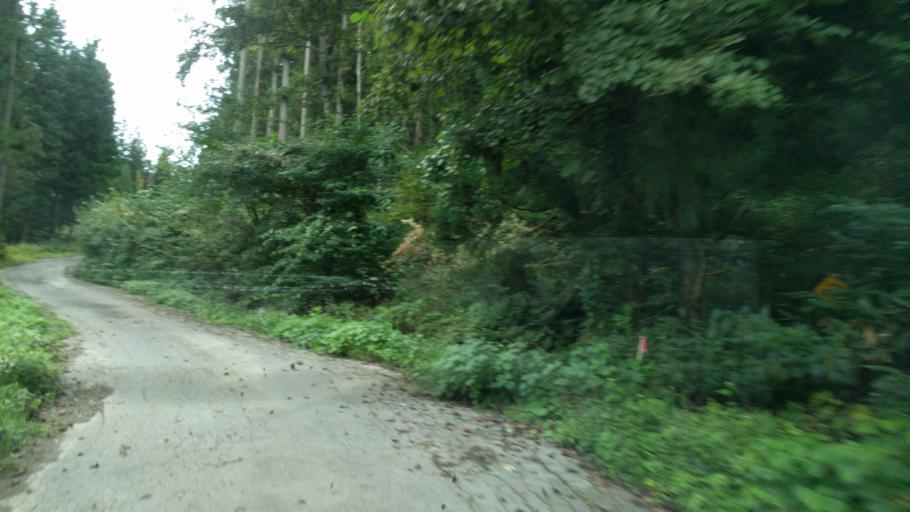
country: JP
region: Fukushima
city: Kitakata
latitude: 37.5217
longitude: 139.7595
